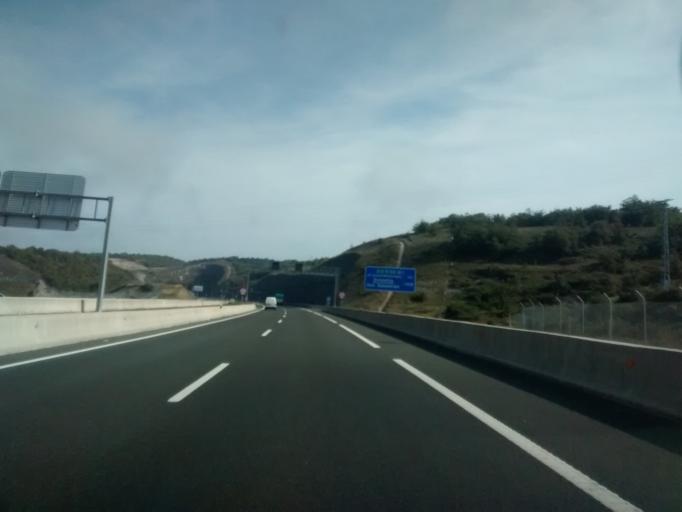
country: ES
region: Basque Country
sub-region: Provincia de Alava
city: Gasteiz / Vitoria
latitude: 42.9295
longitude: -2.6383
